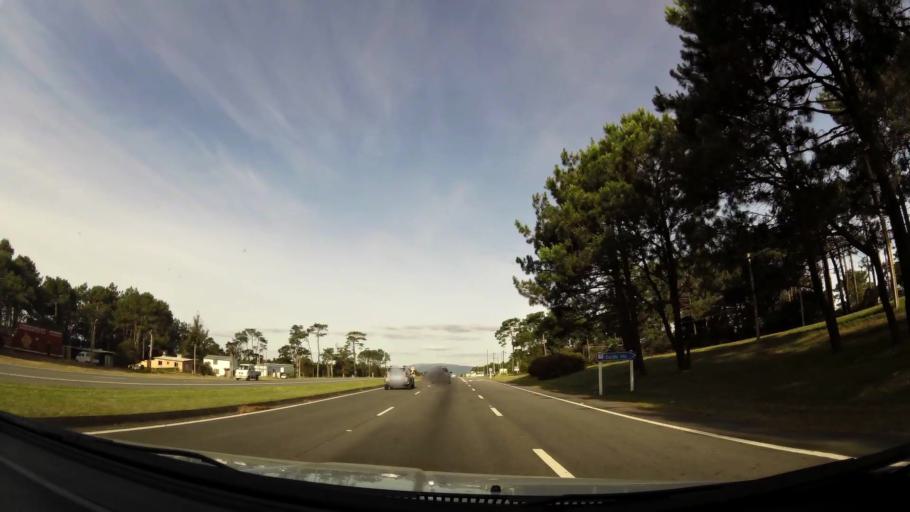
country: UY
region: Lavalleja
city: Solis de Mataojo
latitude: -34.7836
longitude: -55.4926
